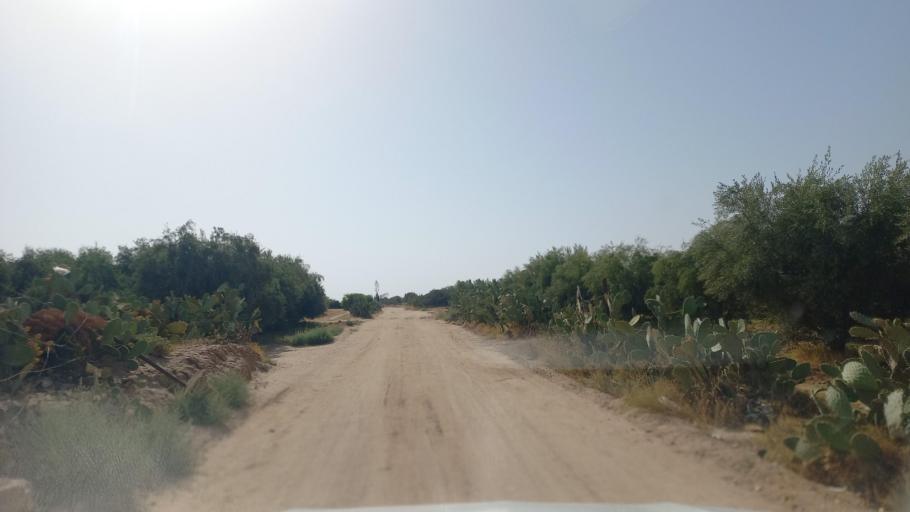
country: TN
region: Al Qasrayn
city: Kasserine
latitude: 35.2504
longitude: 9.0311
